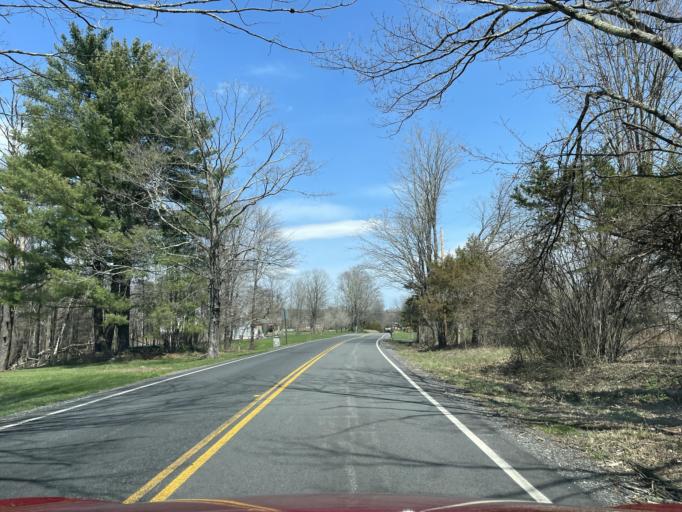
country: US
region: New York
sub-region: Ulster County
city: Manorville
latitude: 42.1333
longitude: -74.0168
